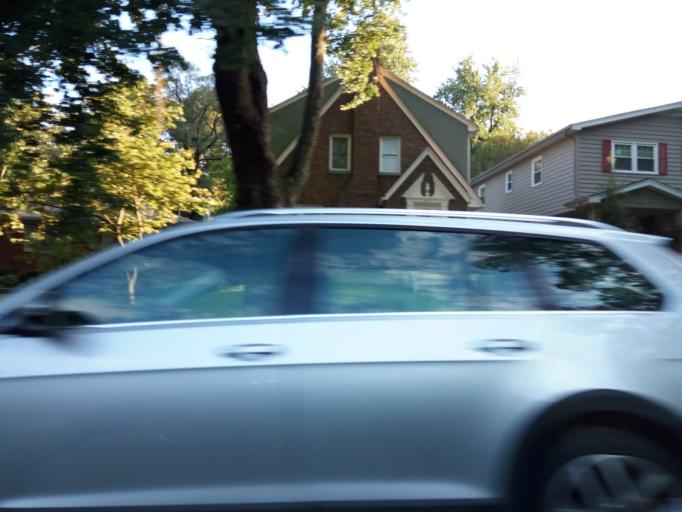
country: US
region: Kentucky
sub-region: Jefferson County
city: Audubon Park
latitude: 38.2058
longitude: -85.7257
